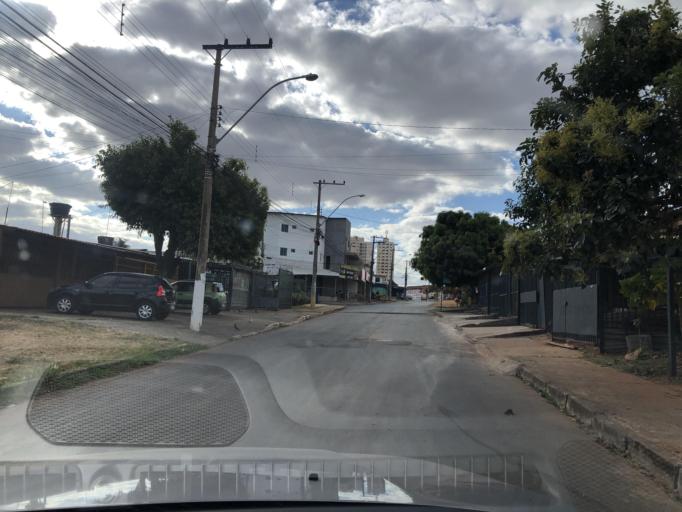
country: BR
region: Federal District
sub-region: Brasilia
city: Brasilia
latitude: -15.8886
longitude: -48.0903
